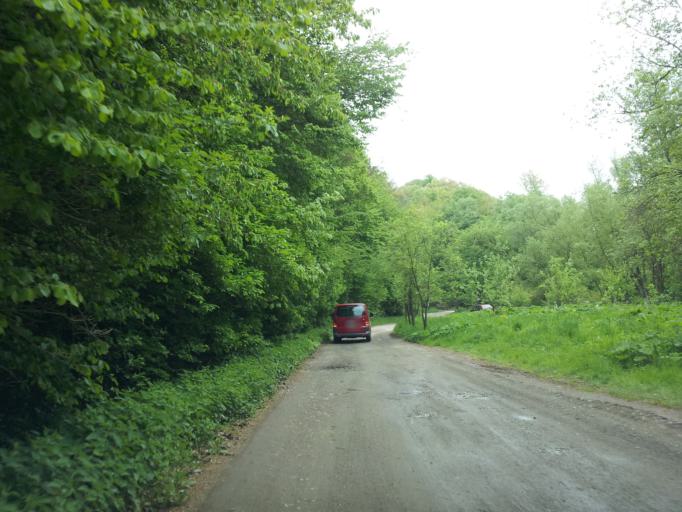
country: HU
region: Baranya
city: Hosszuheteny
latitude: 46.1841
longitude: 18.3537
